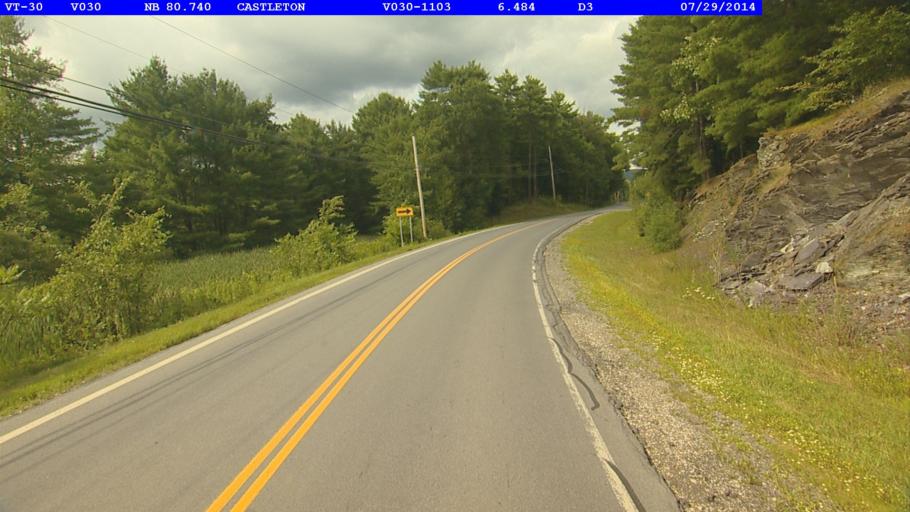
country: US
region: Vermont
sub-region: Rutland County
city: Castleton
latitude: 43.6781
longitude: -73.1913
